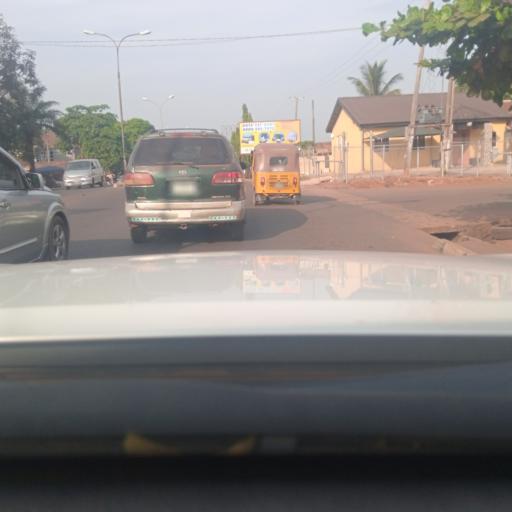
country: NG
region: Enugu
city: Enugu
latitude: 6.4505
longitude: 7.5023
